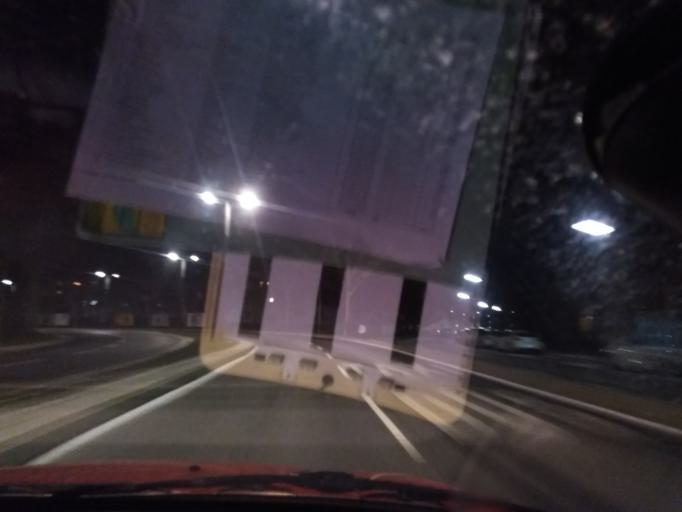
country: AT
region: Vienna
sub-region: Wien Stadt
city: Vienna
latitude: 48.2032
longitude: 16.3165
